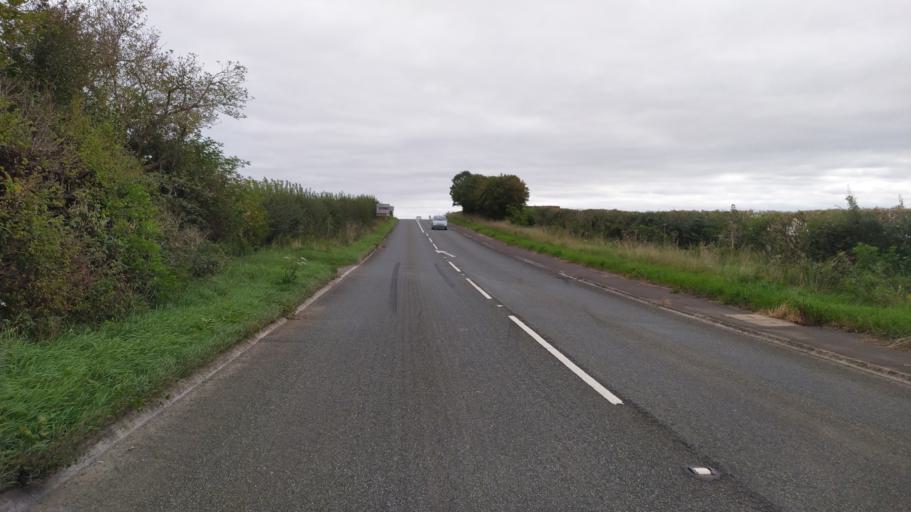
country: GB
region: England
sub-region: Somerset
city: Ilchester
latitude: 51.0094
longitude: -2.6713
